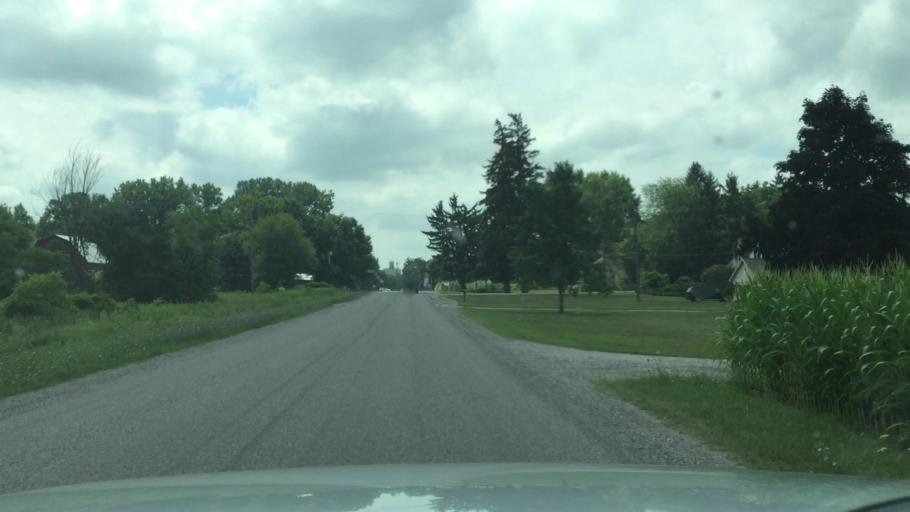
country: US
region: Michigan
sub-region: Saginaw County
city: Birch Run
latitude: 43.2633
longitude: -83.7944
